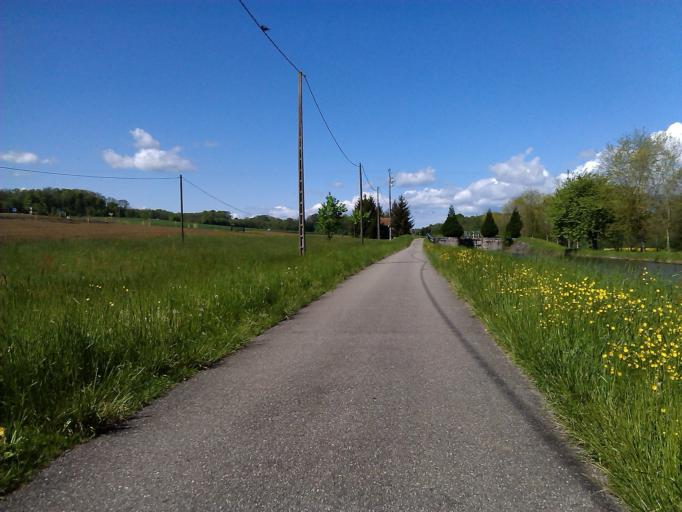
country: FR
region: Alsace
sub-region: Departement du Haut-Rhin
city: Dannemarie
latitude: 47.6351
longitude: 7.0826
